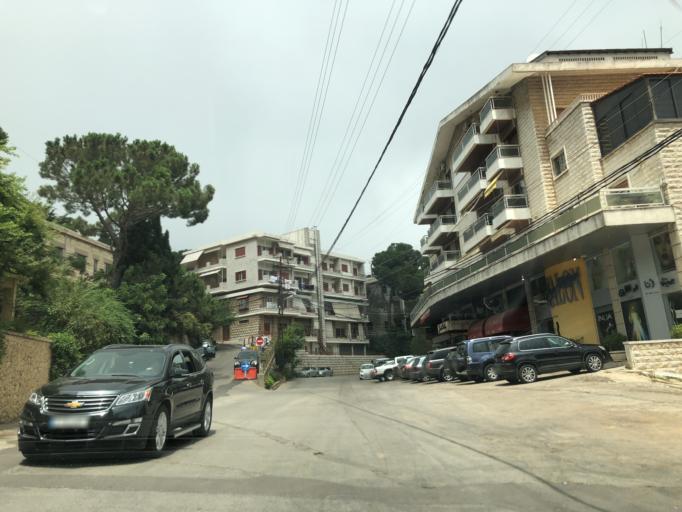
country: LB
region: Mont-Liban
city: Jdaidet el Matn
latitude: 33.8795
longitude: 35.6243
